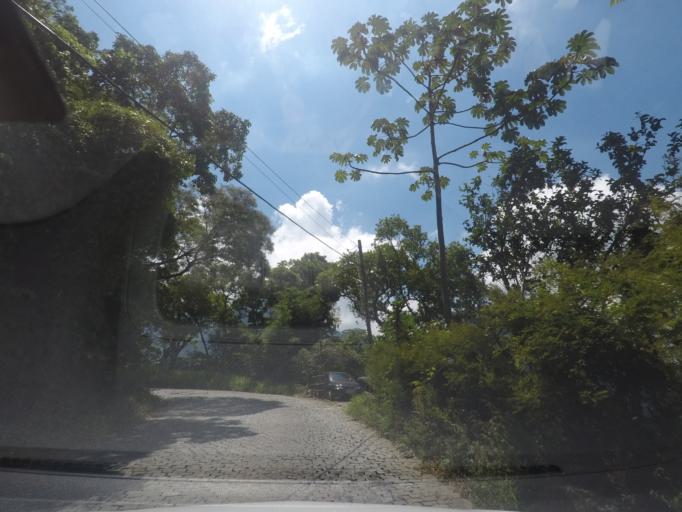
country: BR
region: Rio de Janeiro
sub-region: Petropolis
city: Petropolis
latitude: -22.5390
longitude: -43.1783
